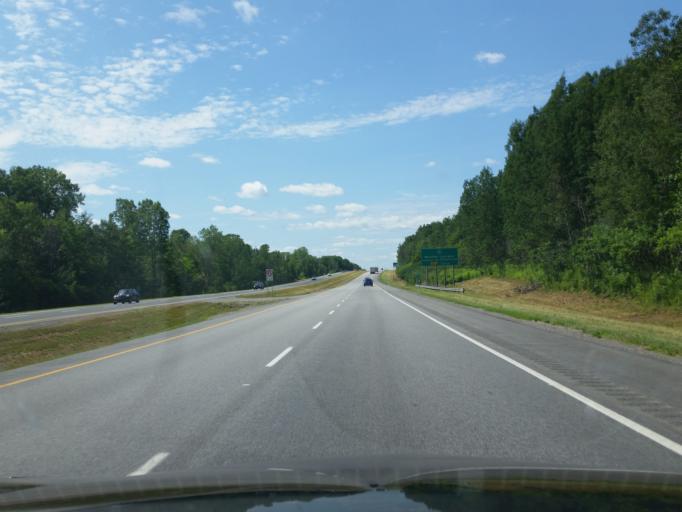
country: CA
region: Quebec
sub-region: Monteregie
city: Hudson
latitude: 45.4482
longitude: -74.2065
